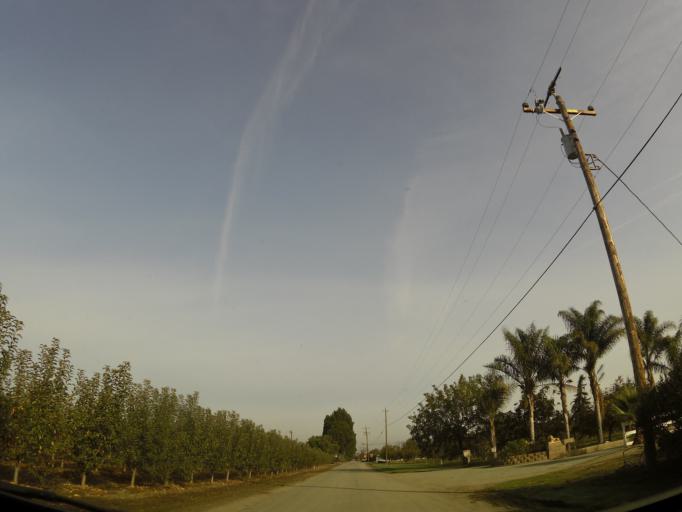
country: US
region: California
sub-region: San Benito County
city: San Juan Bautista
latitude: 36.8475
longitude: -121.4724
